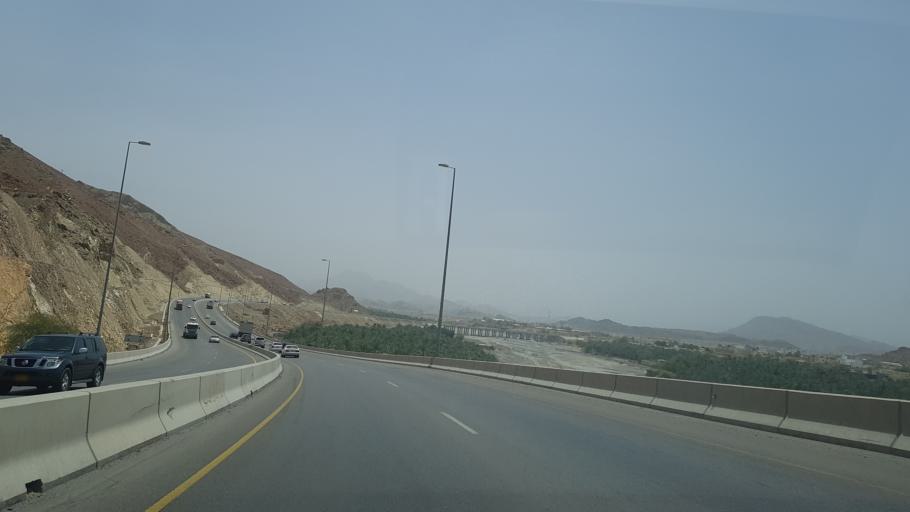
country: OM
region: Muhafazat ad Dakhiliyah
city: Bidbid
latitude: 23.4549
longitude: 58.1172
